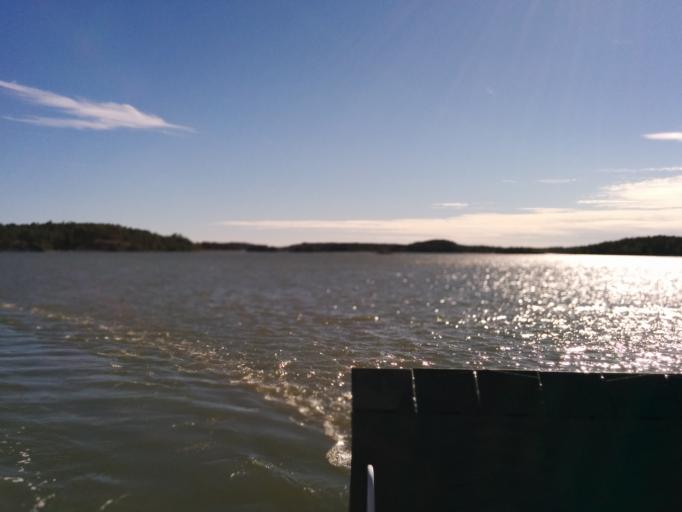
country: FI
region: Varsinais-Suomi
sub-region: Turku
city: Velkua
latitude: 60.4656
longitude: 21.6937
